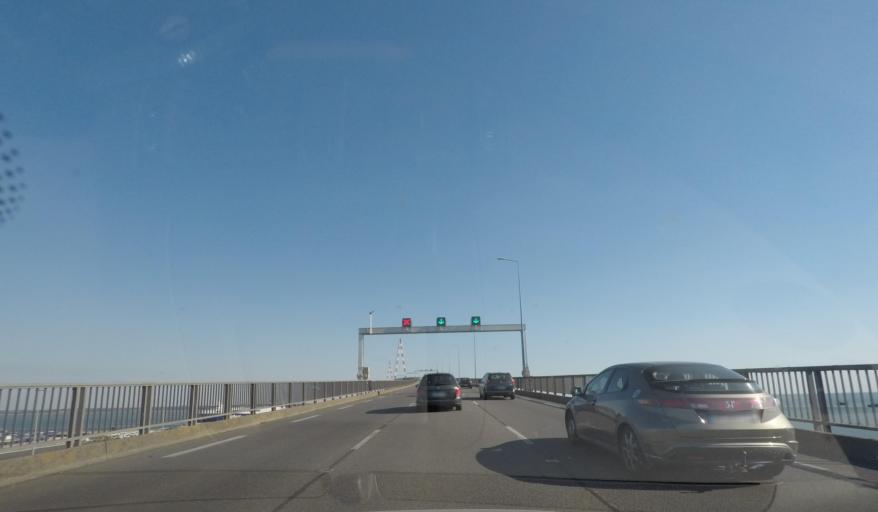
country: FR
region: Pays de la Loire
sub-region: Departement de la Loire-Atlantique
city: Saint-Nazaire
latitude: 47.2921
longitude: -2.1759
